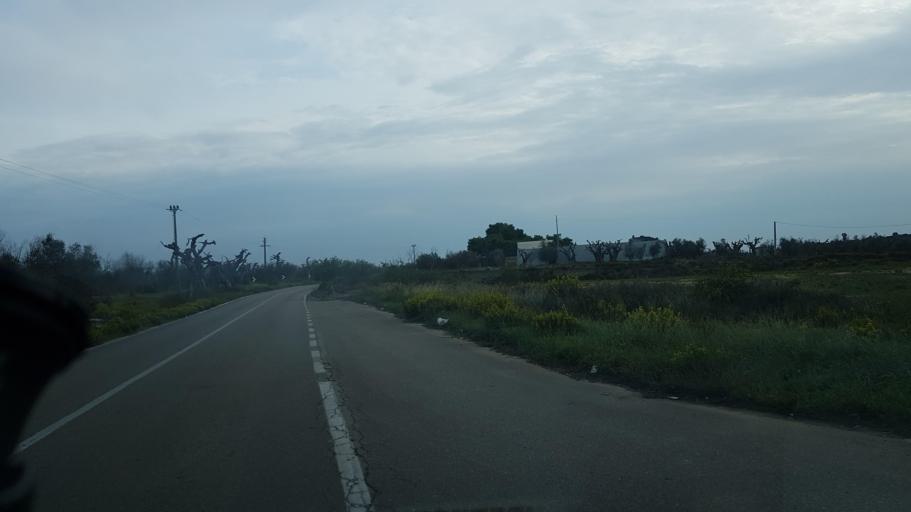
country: IT
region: Apulia
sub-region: Provincia di Lecce
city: Trepuzzi
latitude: 40.4248
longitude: 18.0731
